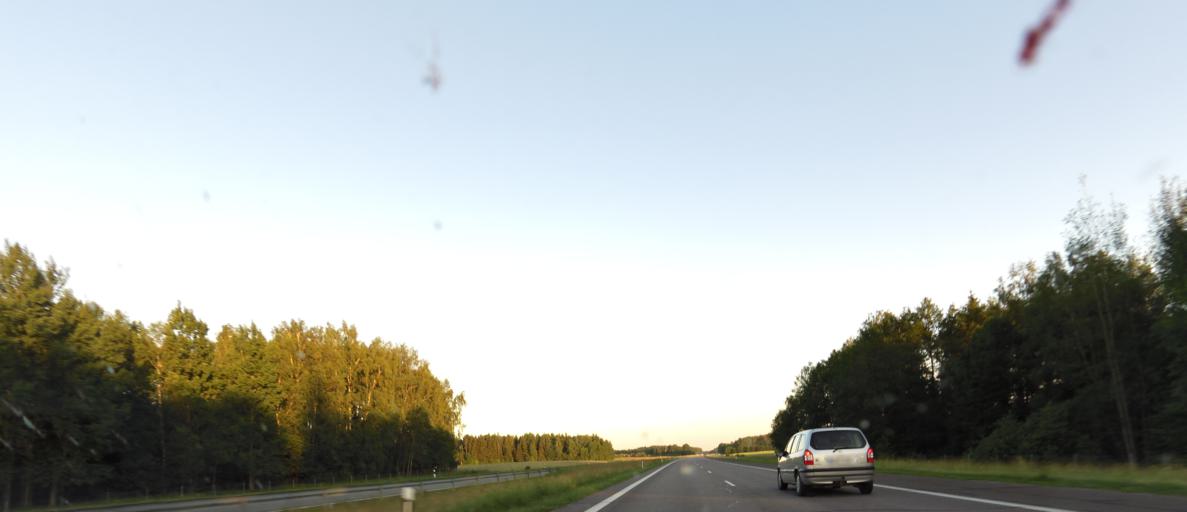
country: LT
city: Sirvintos
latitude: 55.0537
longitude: 24.8914
